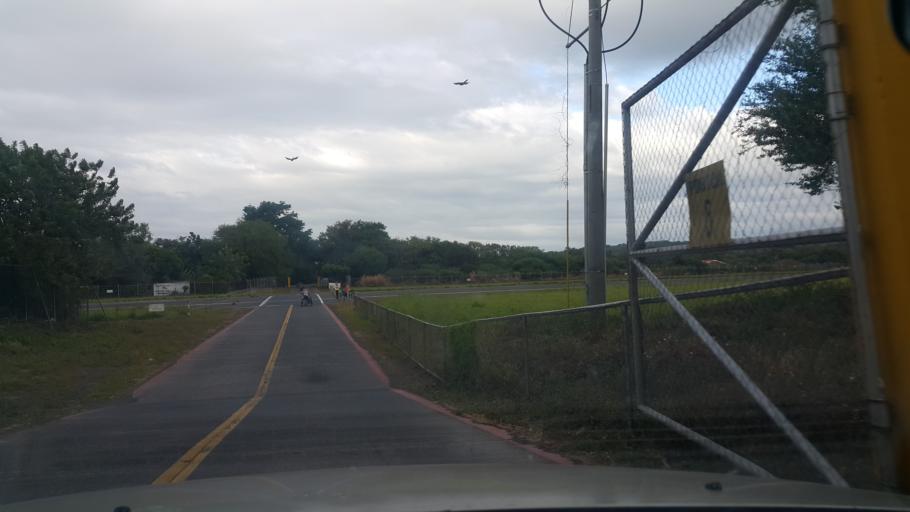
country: NI
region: Rivas
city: Moyogalpa
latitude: 11.5229
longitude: -85.7034
